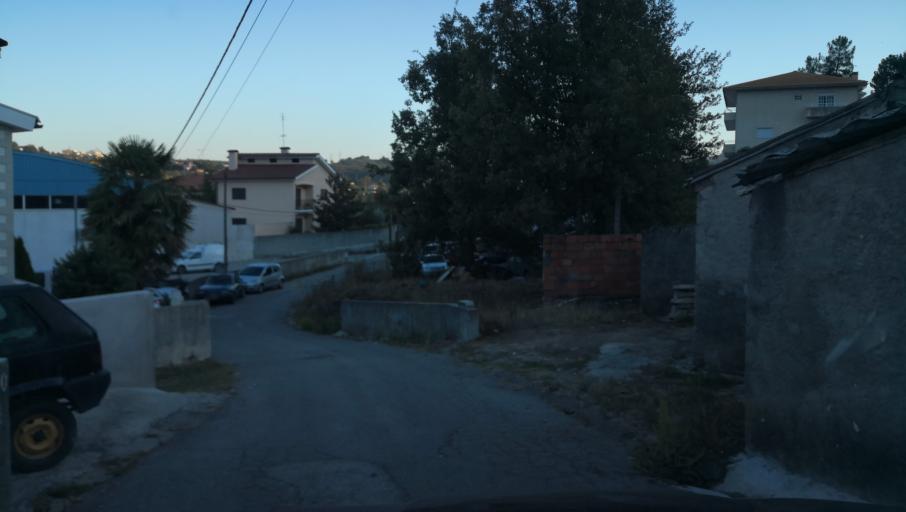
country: PT
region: Vila Real
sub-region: Vila Real
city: Vila Real
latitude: 41.3063
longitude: -7.7612
